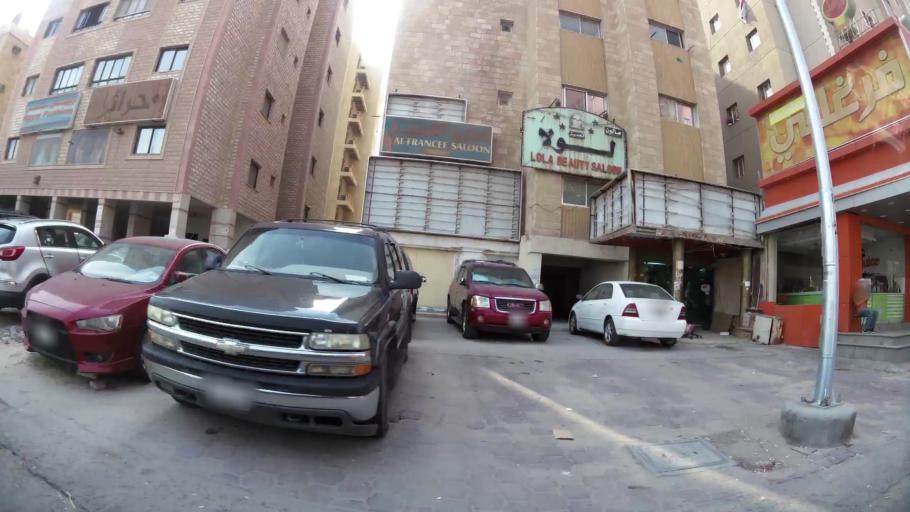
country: KW
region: Al Farwaniyah
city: Al Farwaniyah
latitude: 29.2770
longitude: 47.9593
